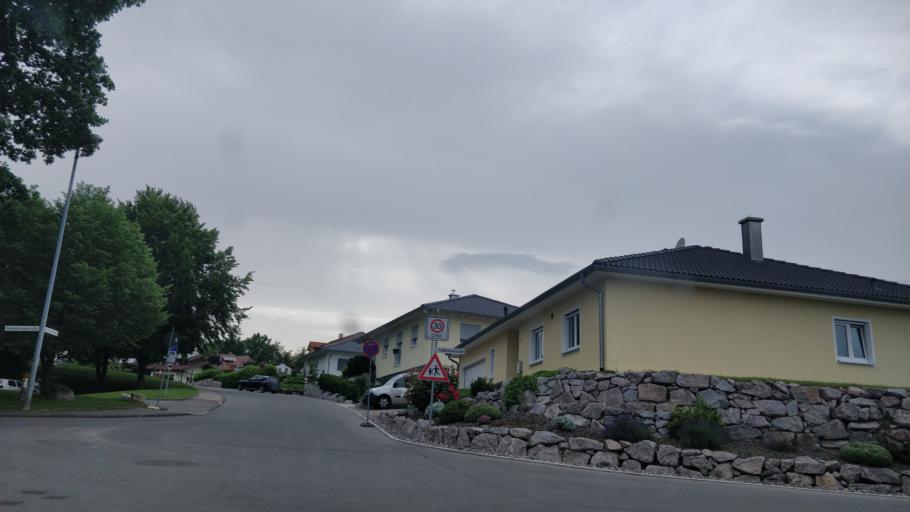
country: DE
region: Baden-Wuerttemberg
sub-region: Freiburg Region
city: Lottstetten
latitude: 47.6316
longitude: 8.5787
